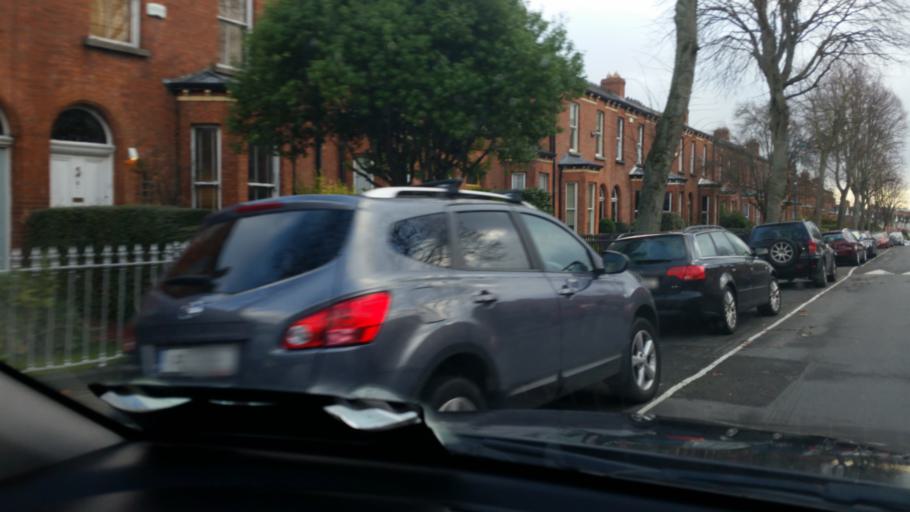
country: IE
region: Leinster
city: Cabra
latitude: 53.3584
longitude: -6.2800
